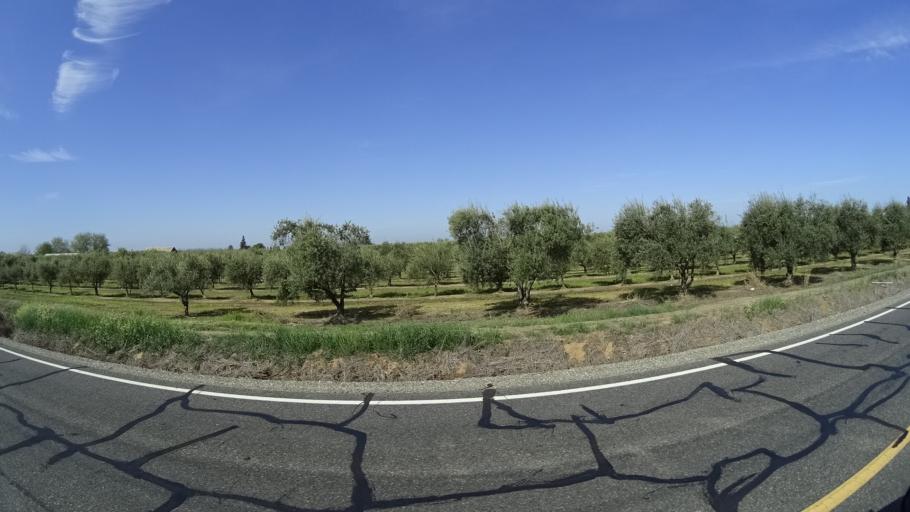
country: US
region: California
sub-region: Glenn County
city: Hamilton City
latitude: 39.6614
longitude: -122.0082
